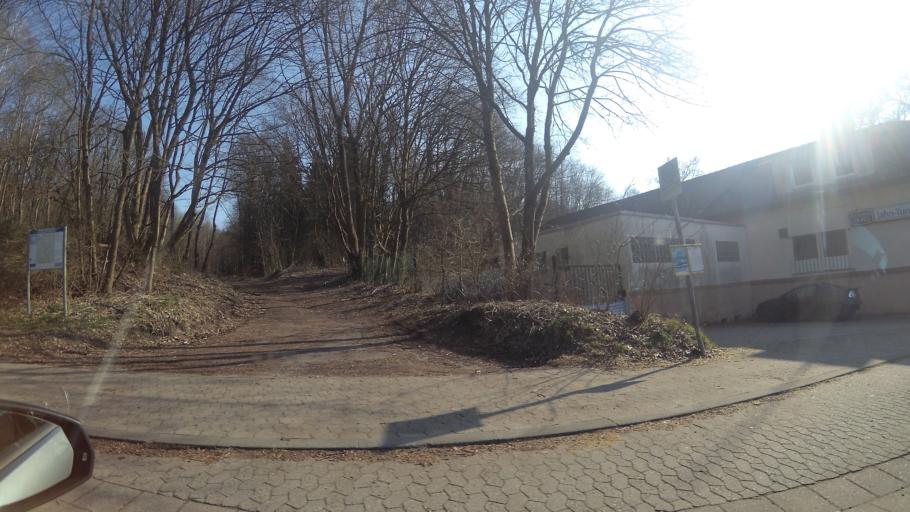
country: DE
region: Saarland
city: Sulzbach
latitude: 49.3021
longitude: 7.0726
